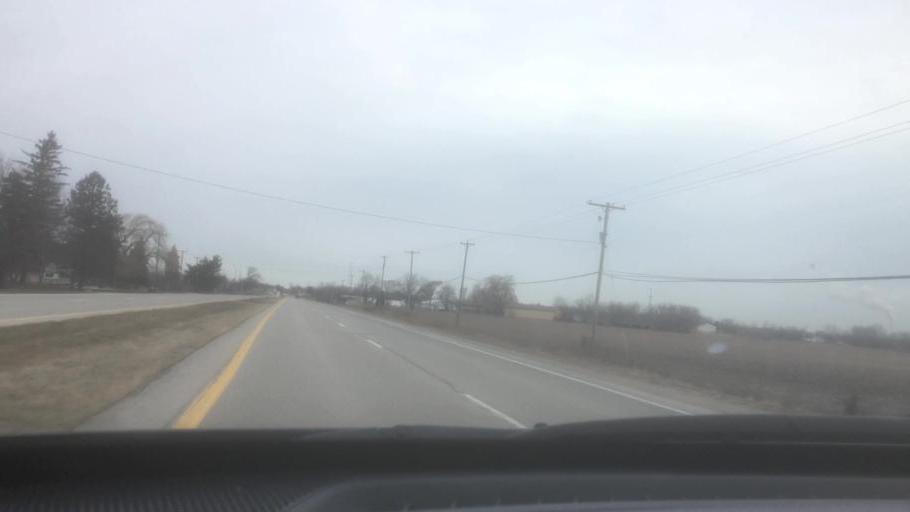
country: US
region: Michigan
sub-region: Bay County
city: Essexville
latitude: 43.5688
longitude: -83.8472
